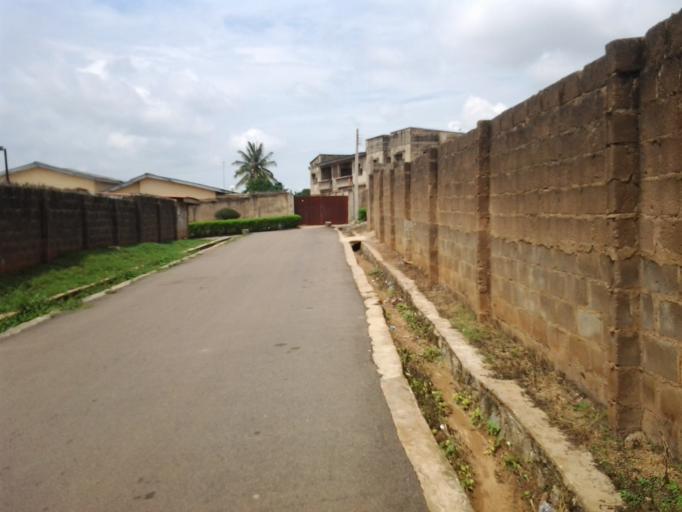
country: NG
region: Oyo
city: Ibadan
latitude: 7.4358
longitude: 3.9486
